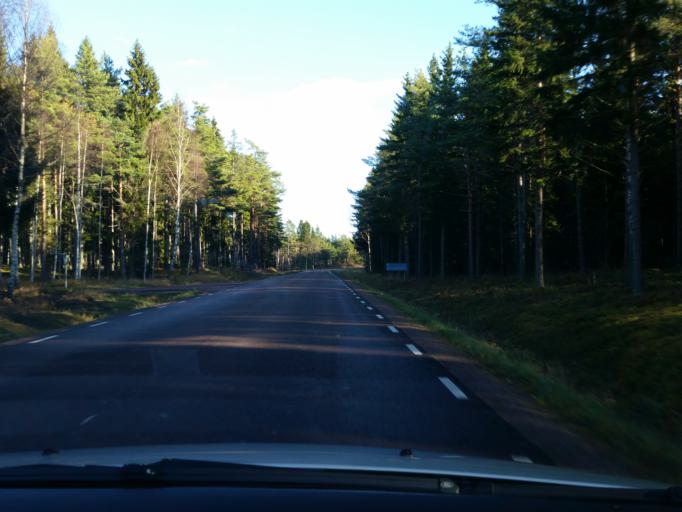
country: AX
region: Alands landsbygd
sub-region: Jomala
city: Jomala
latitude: 60.1586
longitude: 19.8893
